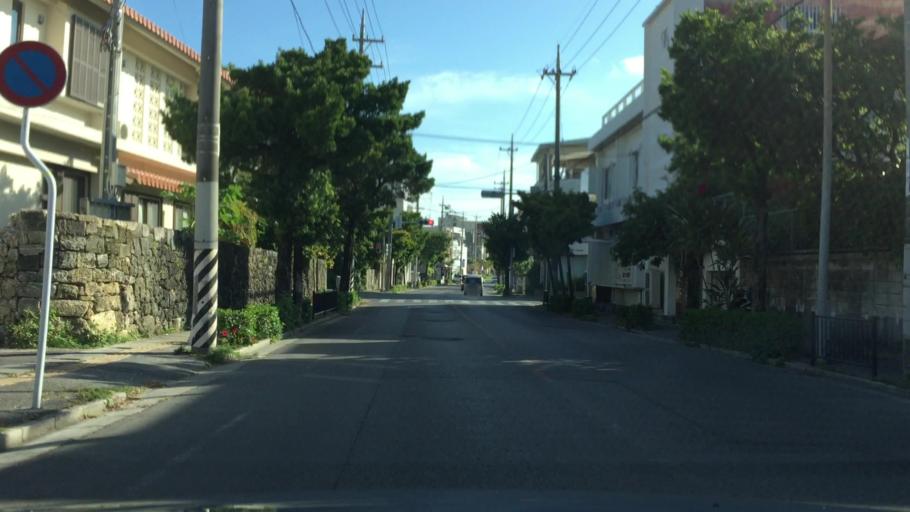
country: JP
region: Okinawa
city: Ishigaki
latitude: 24.3442
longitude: 124.1556
